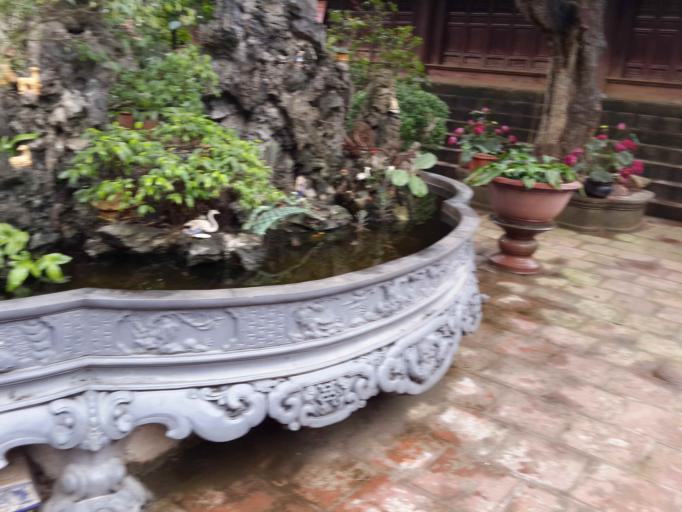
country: VN
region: Ha Noi
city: Son Tay
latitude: 21.1619
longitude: 105.4674
